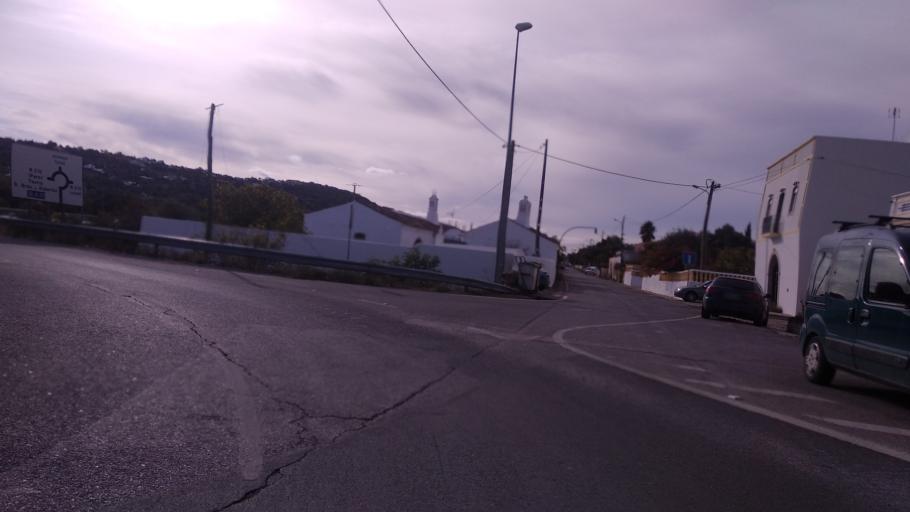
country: PT
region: Faro
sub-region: Sao Bras de Alportel
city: Sao Bras de Alportel
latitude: 37.1516
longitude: -7.9267
